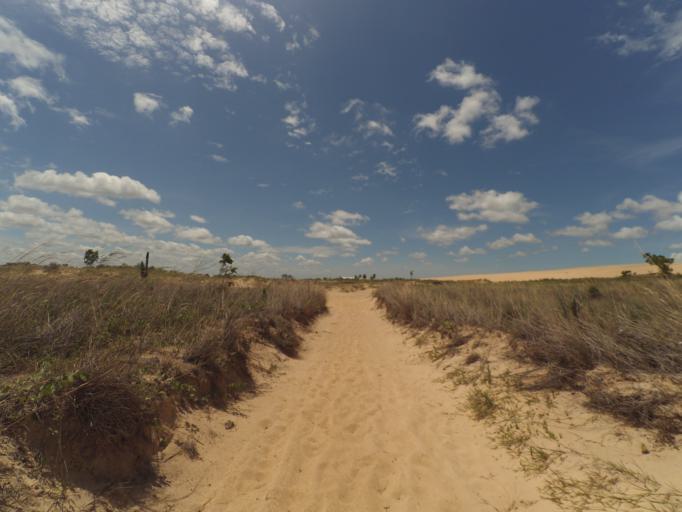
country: BO
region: Santa Cruz
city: Santa Cruz de la Sierra
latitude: -17.9368
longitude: -63.1580
